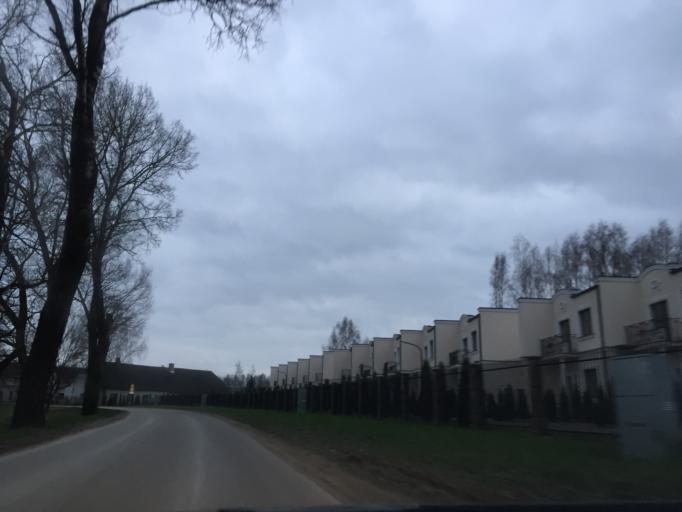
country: LV
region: Stopini
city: Ulbroka
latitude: 56.9383
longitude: 24.2858
